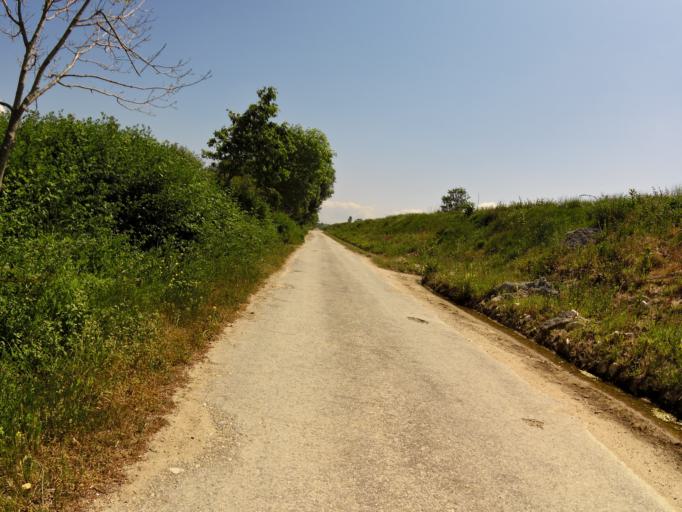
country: PT
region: Coimbra
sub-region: Montemor-O-Velho
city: Montemor-o-Velho
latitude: 40.1485
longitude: -8.7330
